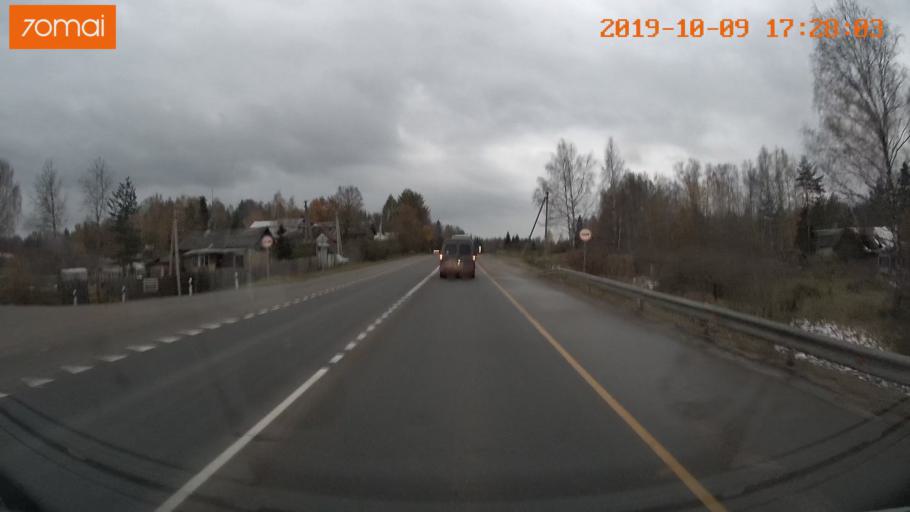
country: RU
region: Ivanovo
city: Furmanov
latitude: 57.1613
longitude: 41.0691
